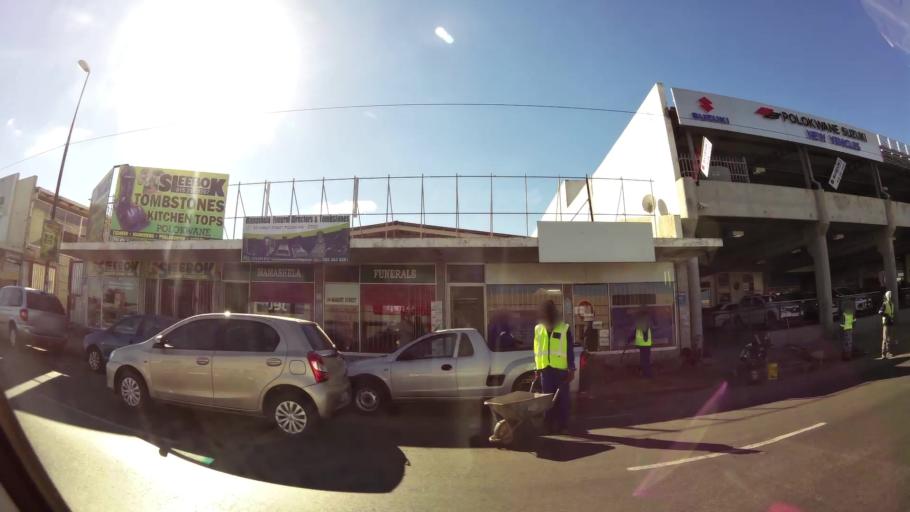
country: ZA
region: Limpopo
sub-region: Capricorn District Municipality
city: Polokwane
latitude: -23.9033
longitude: 29.4503
